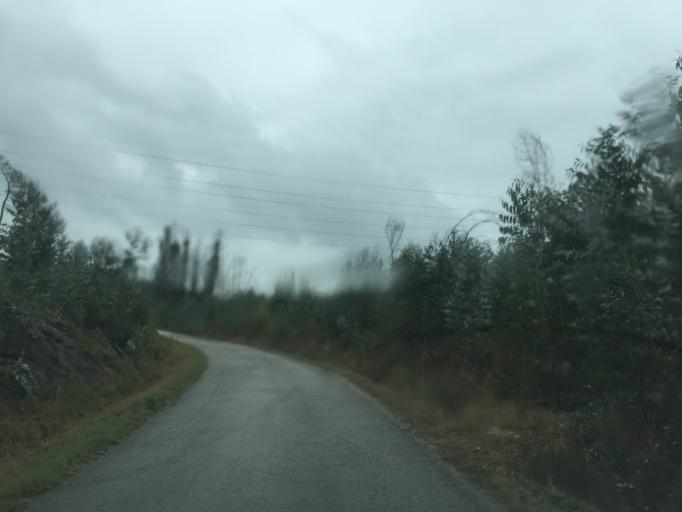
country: PT
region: Coimbra
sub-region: Figueira da Foz
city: Lavos
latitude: 40.0783
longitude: -8.7970
